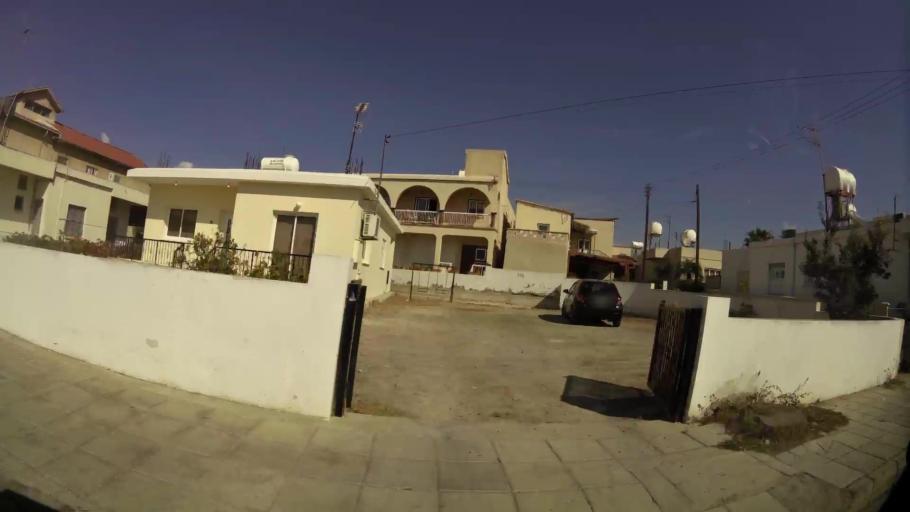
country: CY
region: Larnaka
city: Aradippou
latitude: 34.9525
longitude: 33.5875
